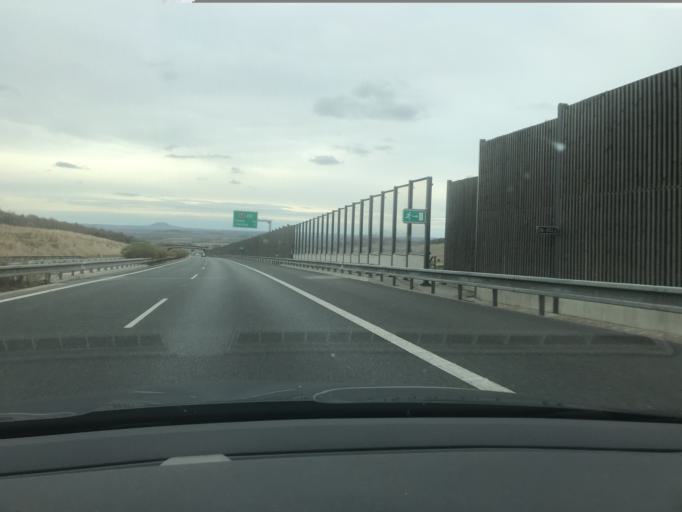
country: CZ
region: Ustecky
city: Velemin
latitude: 50.5233
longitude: 14.0043
